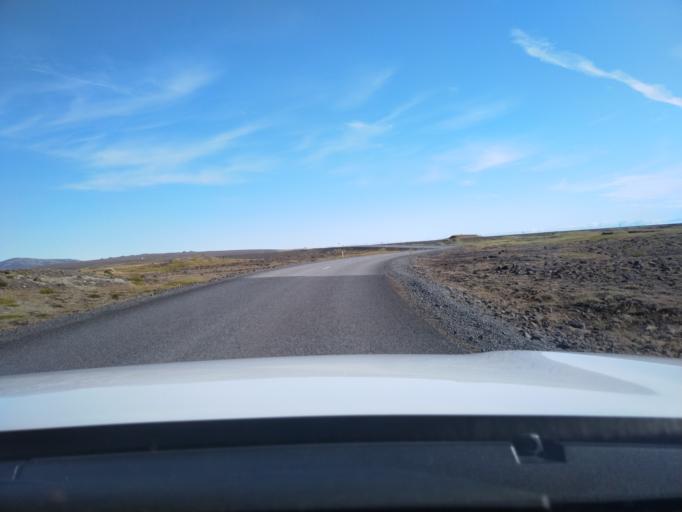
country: IS
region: South
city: THorlakshoefn
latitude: 63.8340
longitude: -21.6724
